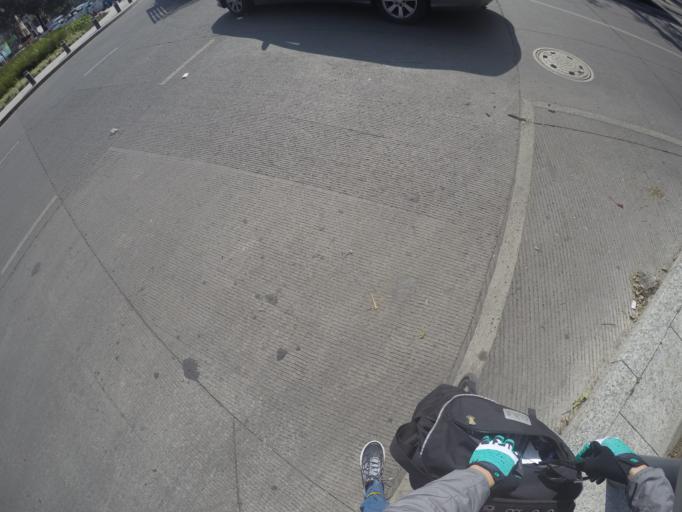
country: MX
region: Mexico
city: Naucalpan de Juarez
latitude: 19.4567
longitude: -99.2252
